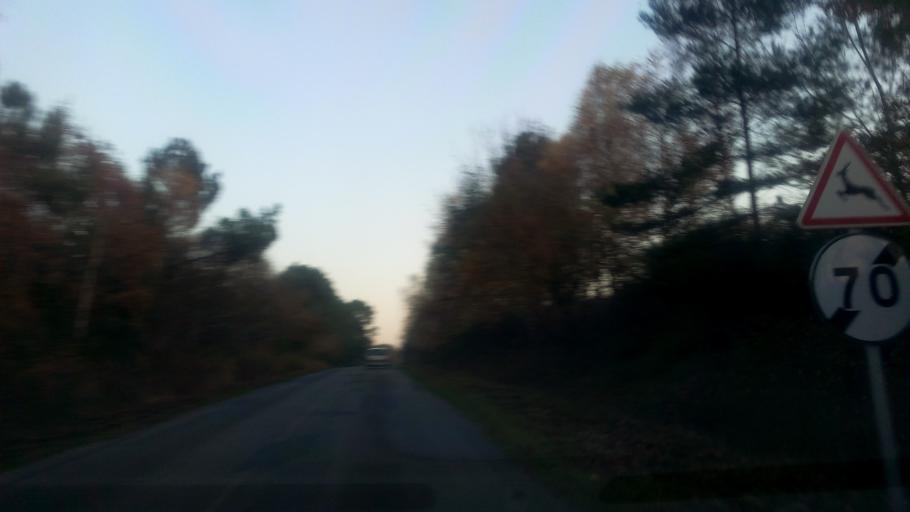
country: FR
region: Brittany
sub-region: Departement d'Ille-et-Vilaine
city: Sixt-sur-Aff
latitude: 47.7460
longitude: -2.0558
